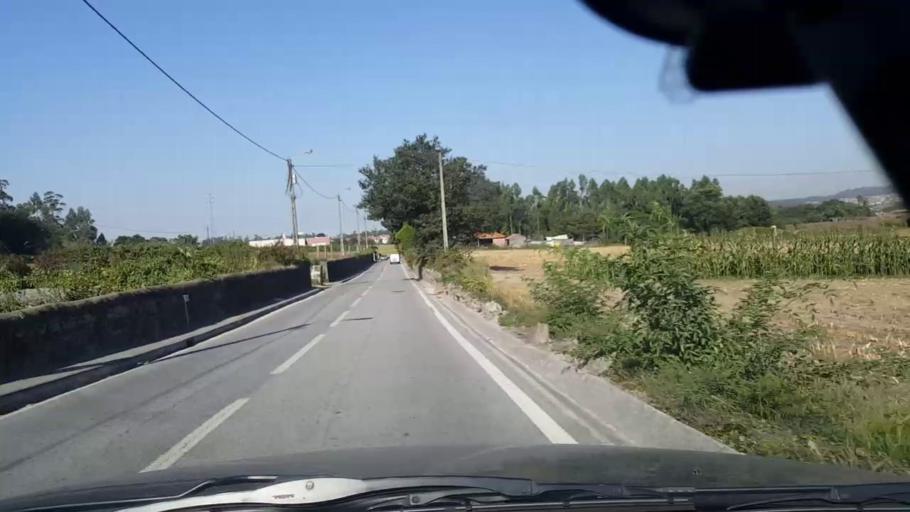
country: PT
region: Porto
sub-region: Vila do Conde
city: Arvore
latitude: 41.3755
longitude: -8.6717
